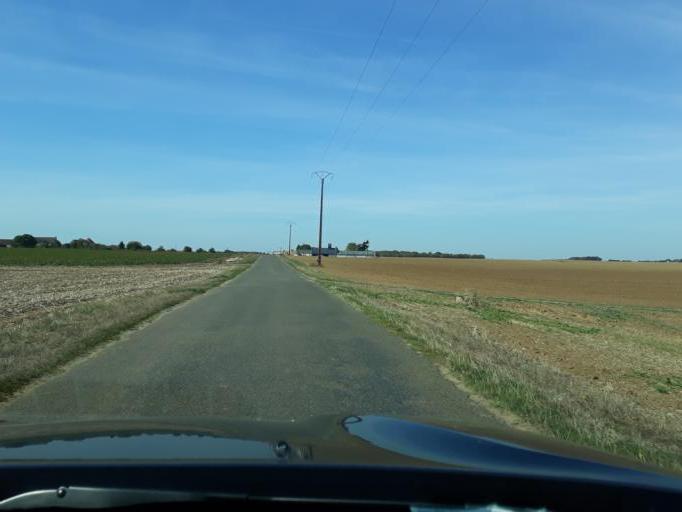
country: FR
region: Centre
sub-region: Departement du Loir-et-Cher
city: Ouzouer-le-Marche
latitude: 47.9422
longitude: 1.5325
